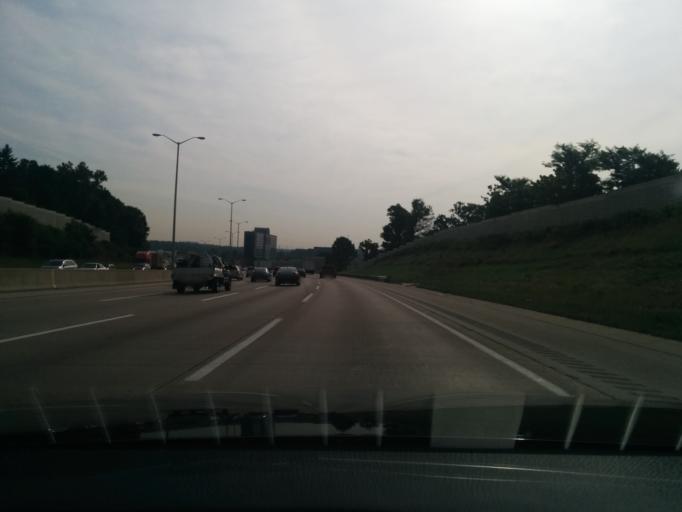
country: US
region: Illinois
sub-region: DuPage County
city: Lisle
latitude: 41.8054
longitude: -88.0865
